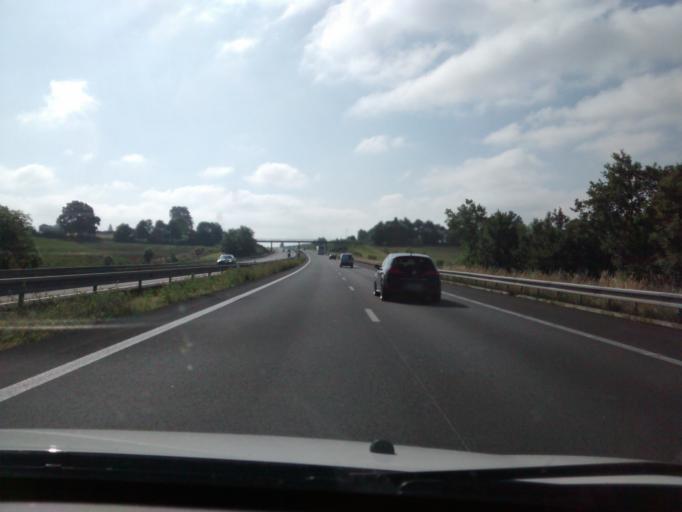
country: FR
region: Pays de la Loire
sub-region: Departement de la Mayenne
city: Sainte-Suzanne
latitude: 48.0406
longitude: -0.3837
